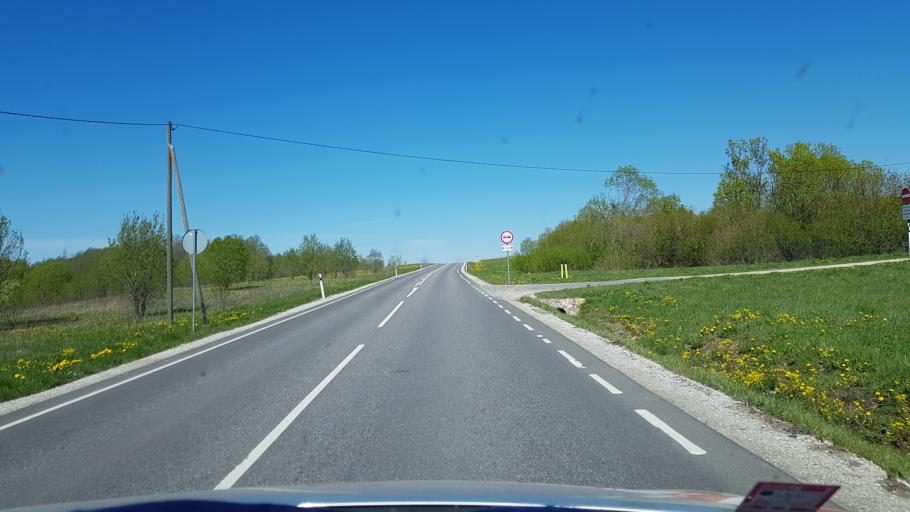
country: EE
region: Ida-Virumaa
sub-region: Narva-Joesuu linn
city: Narva-Joesuu
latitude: 59.4045
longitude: 28.0667
